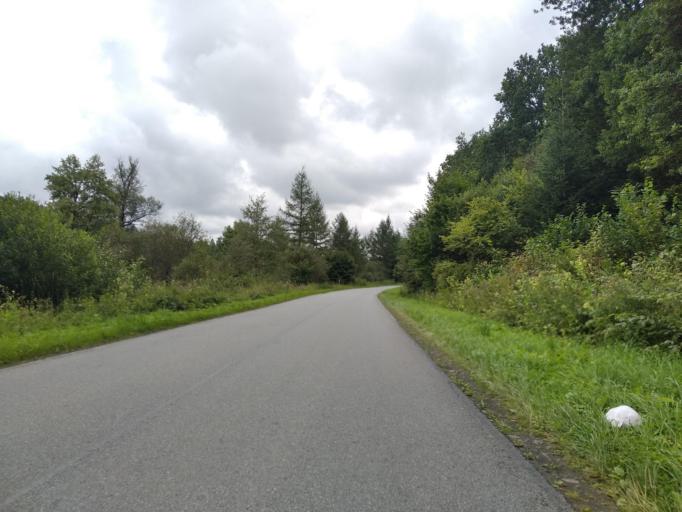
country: PL
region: Subcarpathian Voivodeship
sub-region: Powiat przemyski
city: Bircza
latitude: 49.6872
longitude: 22.4146
